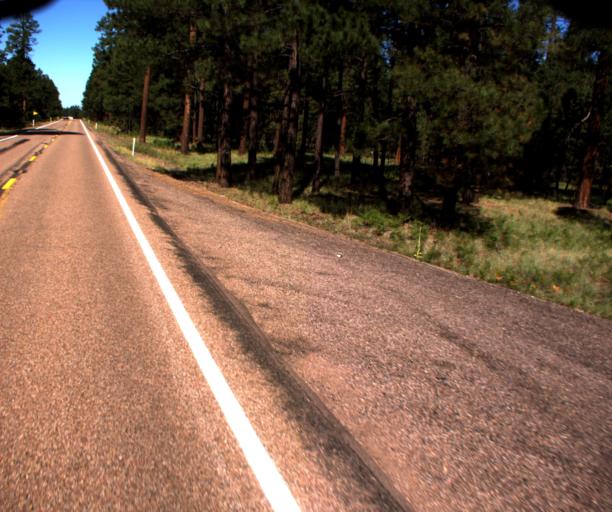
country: US
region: Arizona
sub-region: Navajo County
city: Pinetop-Lakeside
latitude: 34.0528
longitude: -109.7403
